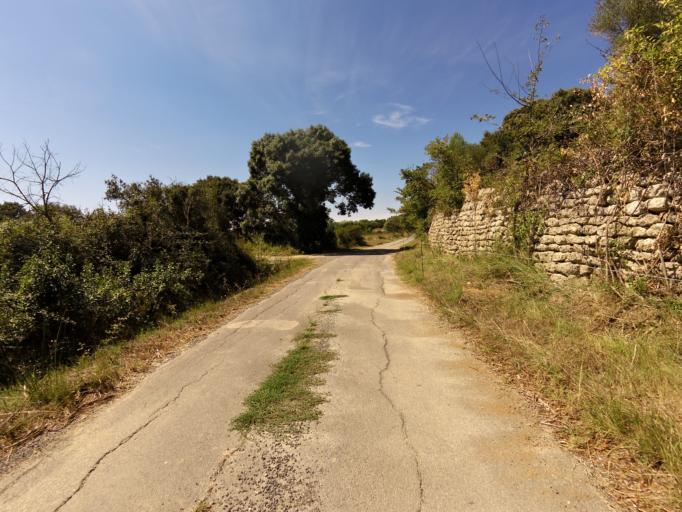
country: FR
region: Languedoc-Roussillon
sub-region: Departement du Gard
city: Aubais
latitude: 43.7558
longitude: 4.1204
